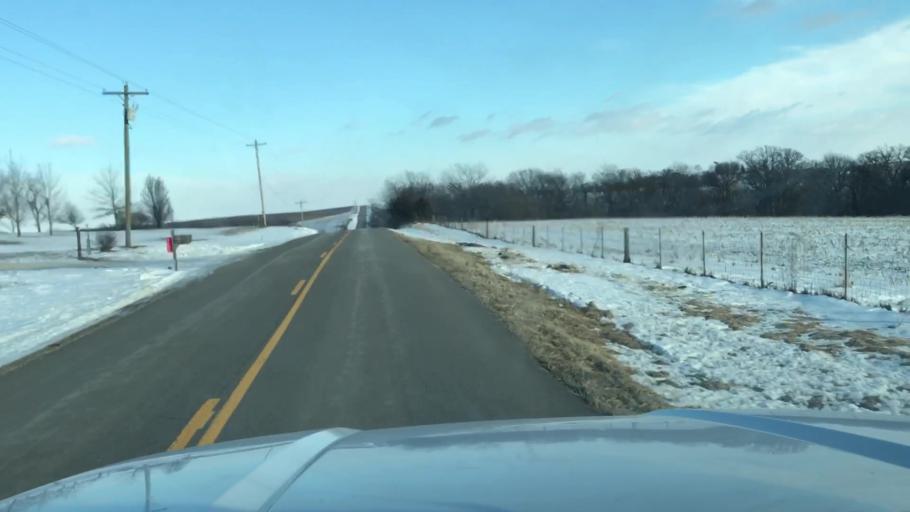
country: US
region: Missouri
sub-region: Holt County
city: Oregon
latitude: 40.1007
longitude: -95.0072
